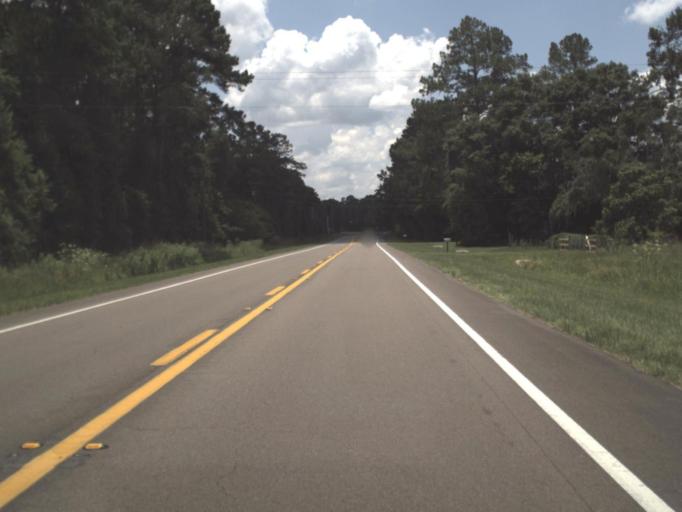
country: US
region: Florida
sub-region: Alachua County
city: Alachua
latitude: 29.8054
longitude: -82.3854
